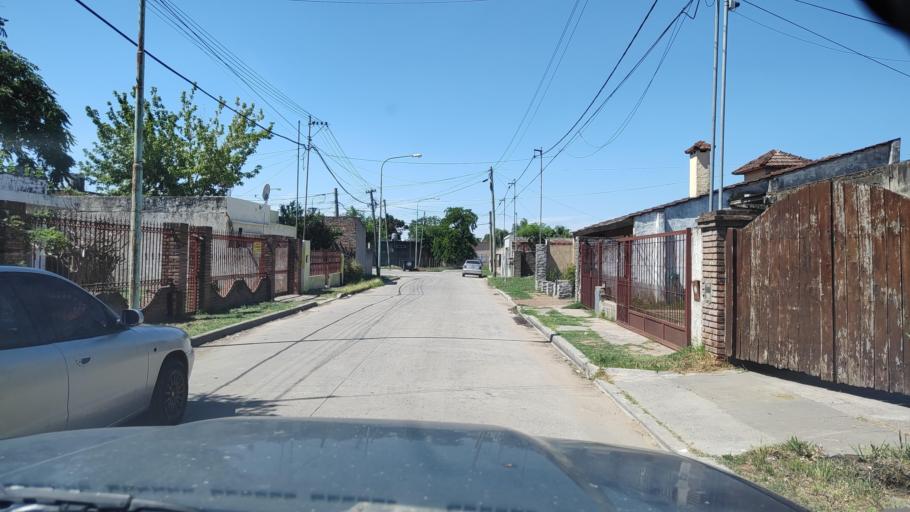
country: AR
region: Buenos Aires
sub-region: Partido de Lujan
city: Lujan
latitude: -34.5749
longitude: -59.1218
